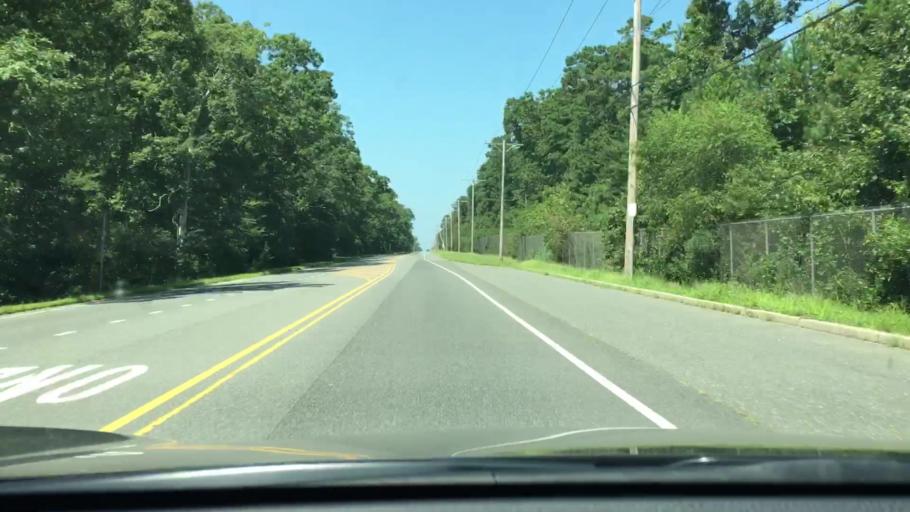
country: US
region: New Jersey
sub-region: Cumberland County
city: Laurel Lake
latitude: 39.3557
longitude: -75.0648
